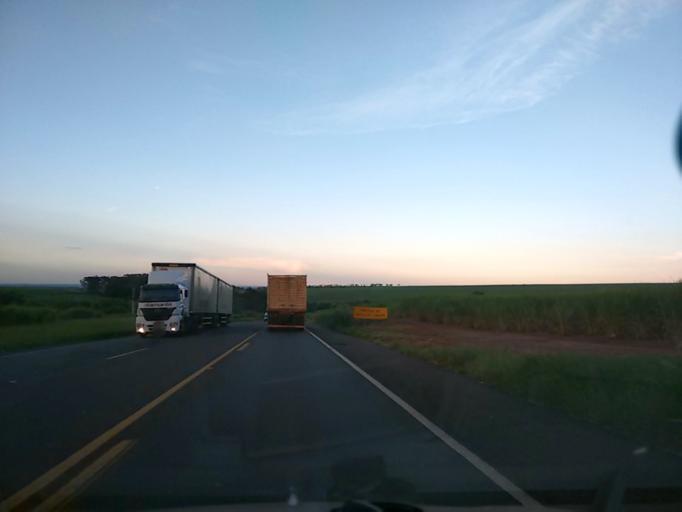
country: BR
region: Sao Paulo
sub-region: Jau
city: Jau
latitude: -22.1505
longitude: -48.4697
